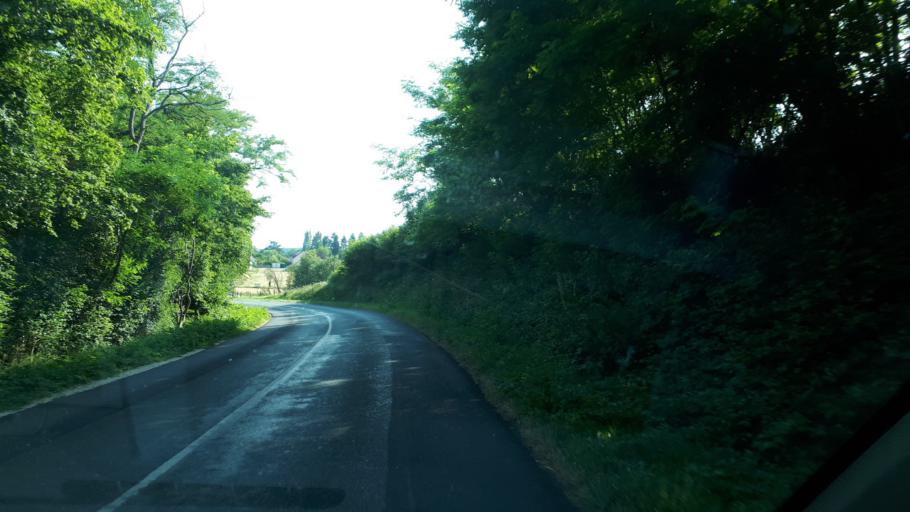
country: FR
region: Centre
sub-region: Departement du Loir-et-Cher
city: Aze
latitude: 47.8568
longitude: 1.0043
